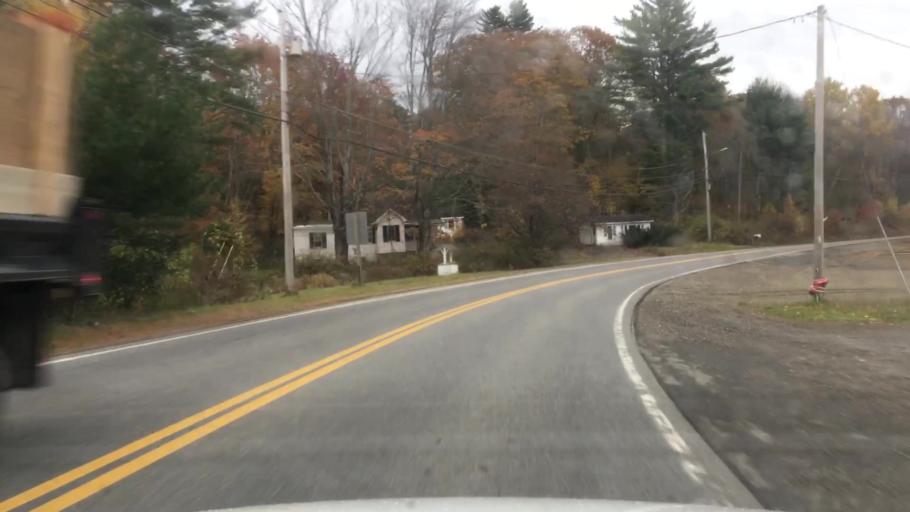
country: US
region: Maine
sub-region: Lincoln County
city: Jefferson
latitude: 44.1998
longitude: -69.4525
